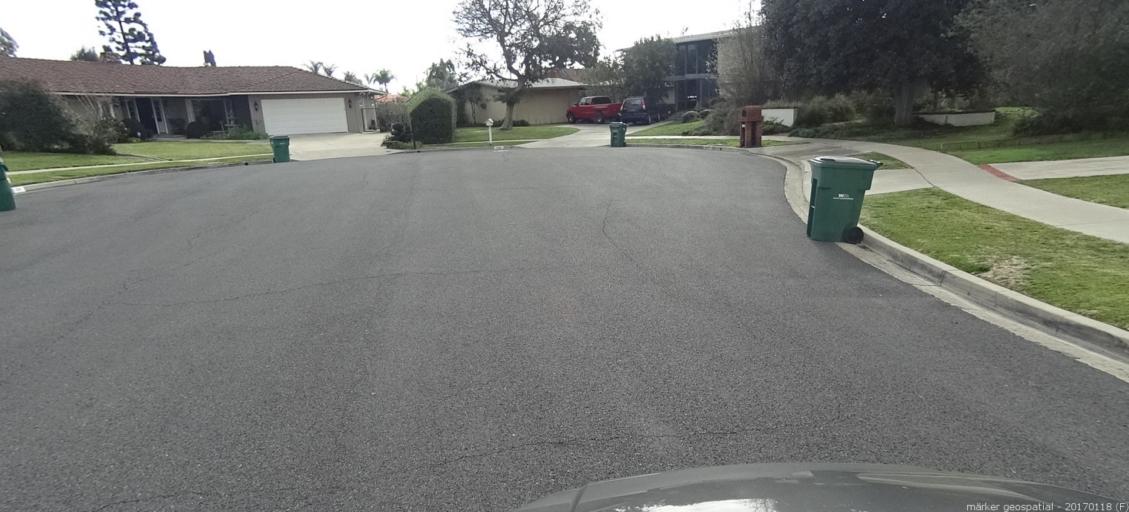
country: US
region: California
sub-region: Orange County
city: North Tustin
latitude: 33.7588
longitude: -117.7999
